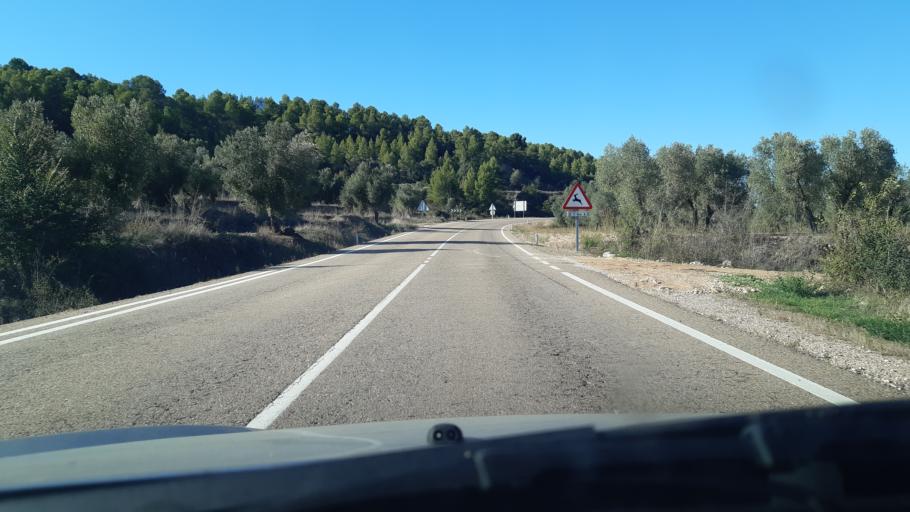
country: ES
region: Aragon
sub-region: Provincia de Teruel
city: Torre del Compte
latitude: 40.8904
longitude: 0.1079
